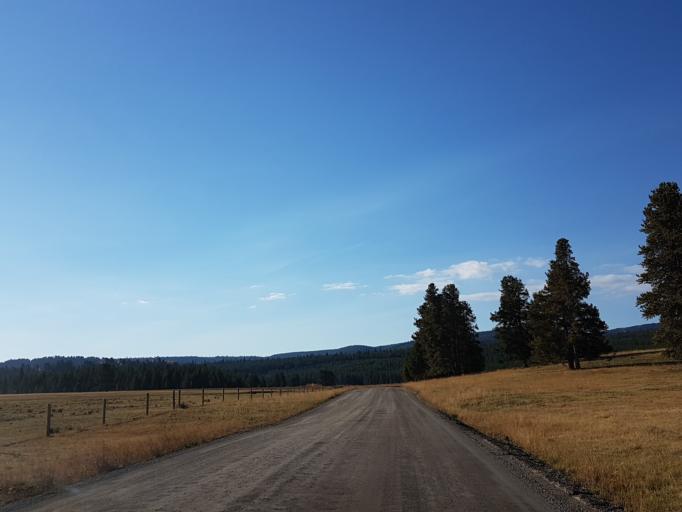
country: US
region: Montana
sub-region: Gallatin County
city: West Yellowstone
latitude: 44.6885
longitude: -111.2136
